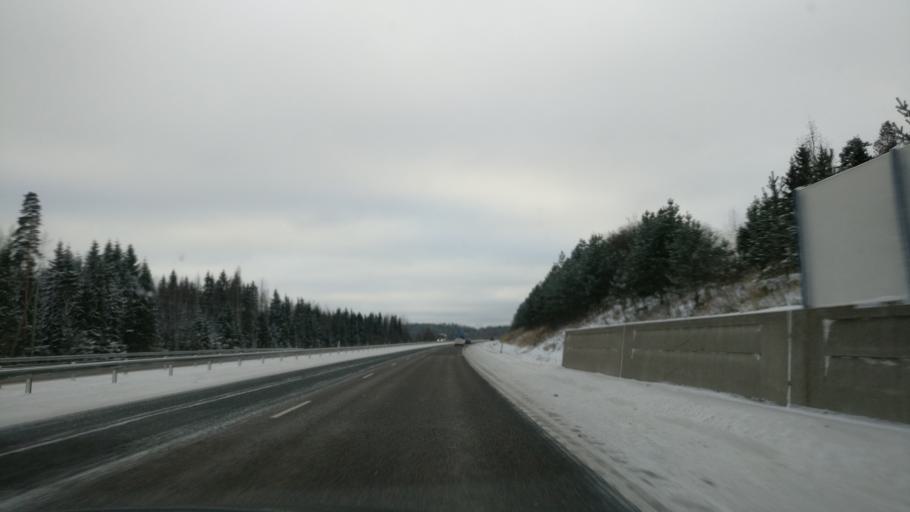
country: FI
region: Paijanne Tavastia
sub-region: Lahti
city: Lahti
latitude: 60.9497
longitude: 25.6880
